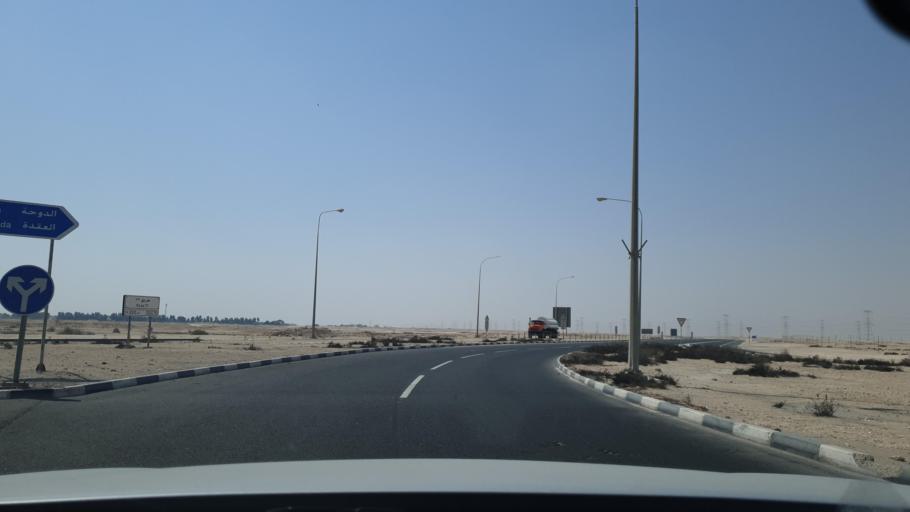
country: QA
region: Al Khawr
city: Al Khawr
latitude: 25.7540
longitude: 51.4750
